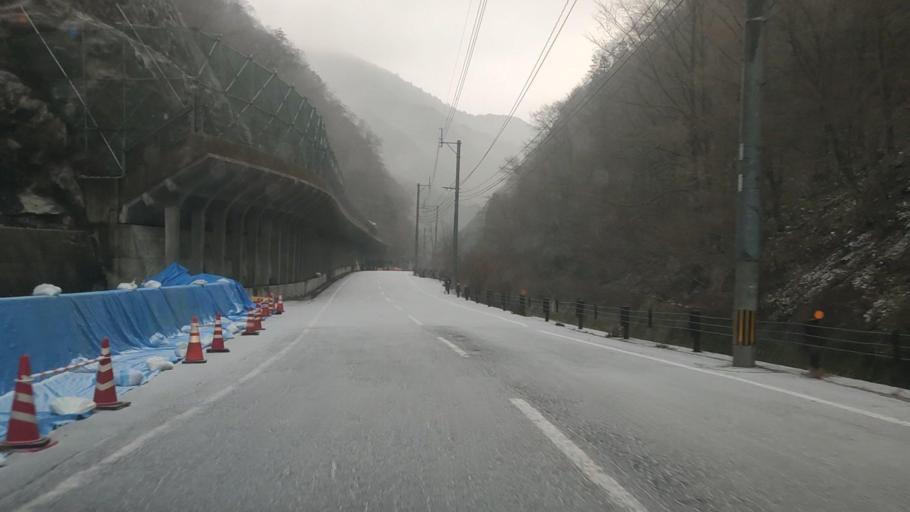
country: JP
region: Kumamoto
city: Matsubase
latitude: 32.5547
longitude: 130.9257
